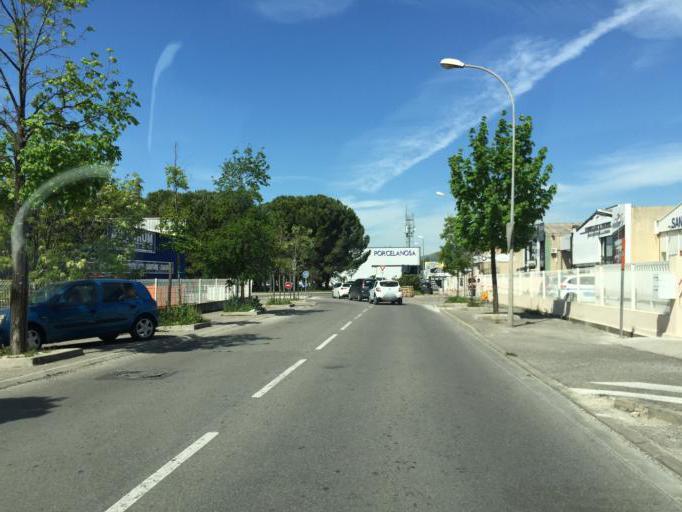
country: FR
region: Provence-Alpes-Cote d'Azur
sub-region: Departement des Bouches-du-Rhone
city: Gemenos
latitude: 43.2882
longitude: 5.6025
